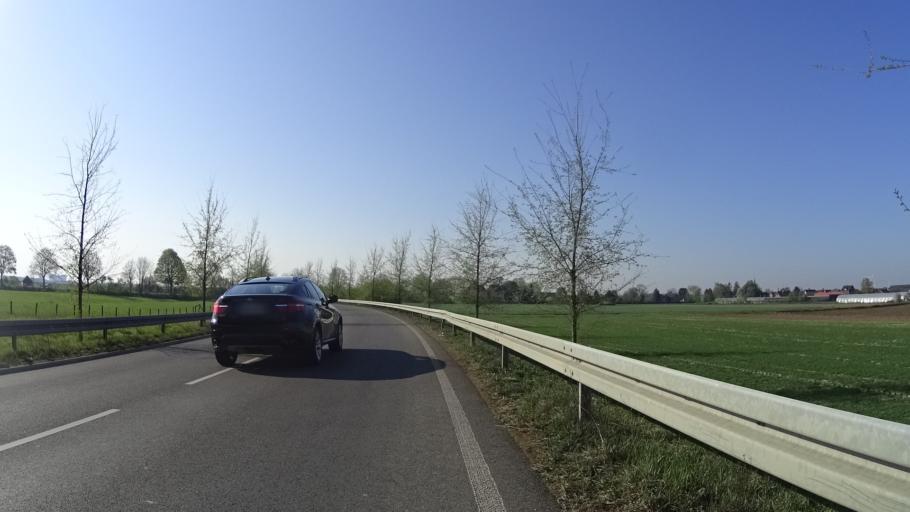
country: DE
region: North Rhine-Westphalia
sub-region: Regierungsbezirk Dusseldorf
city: Wesel
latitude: 51.6378
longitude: 6.5883
